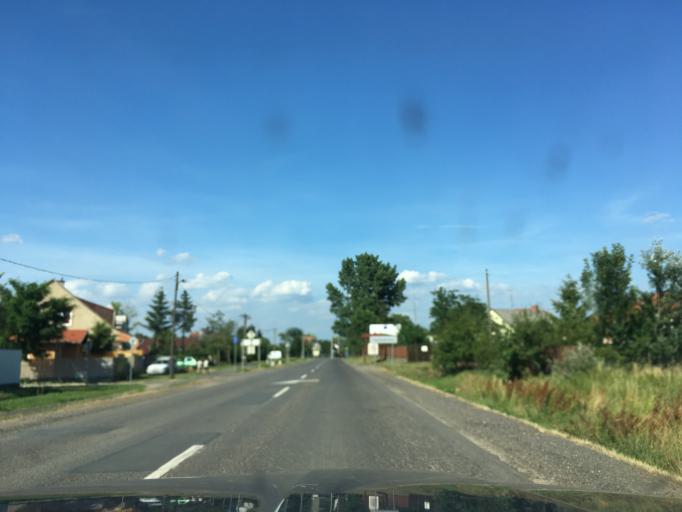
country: HU
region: Hajdu-Bihar
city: Hajdusamson
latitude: 47.5950
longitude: 21.7401
